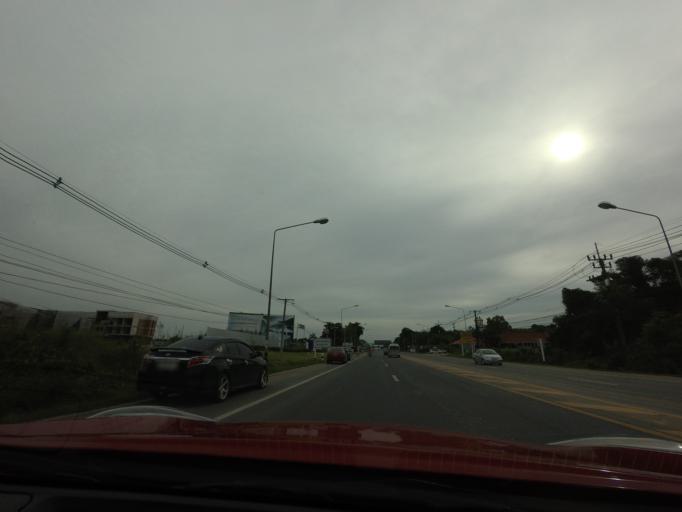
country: TH
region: Songkhla
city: Khlong Hoi Khong
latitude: 6.9416
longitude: 100.4039
